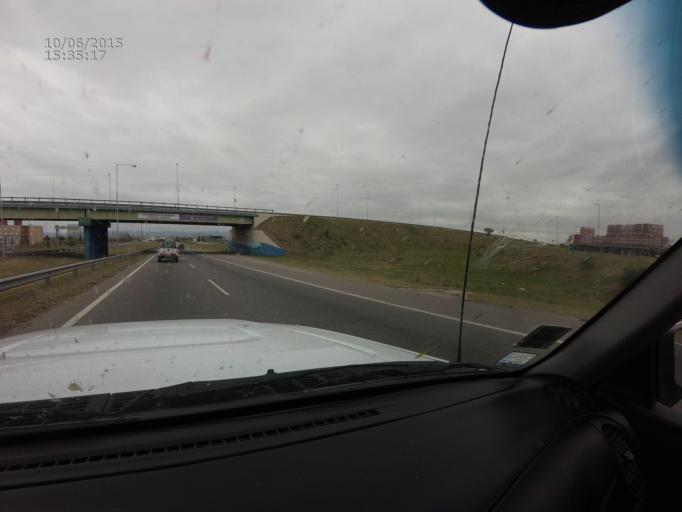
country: AR
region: Cordoba
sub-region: Departamento de Capital
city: Cordoba
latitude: -31.3547
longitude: -64.1889
